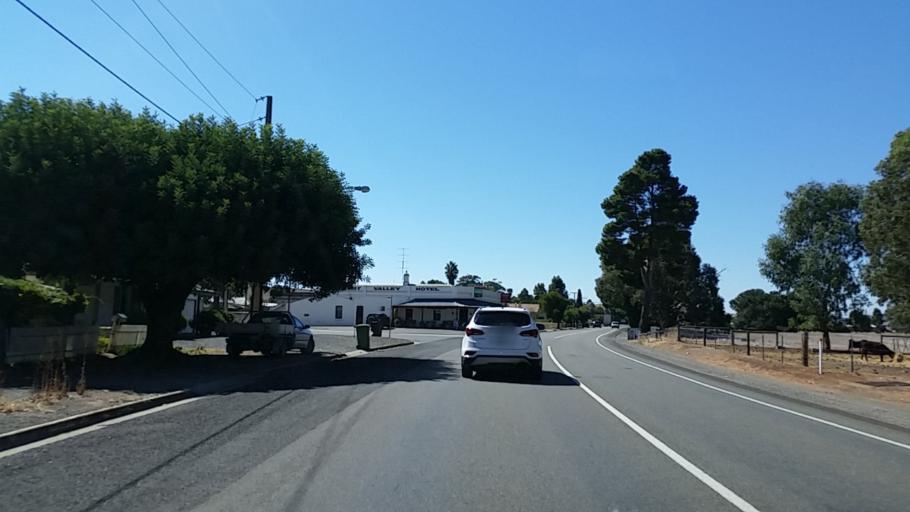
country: AU
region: South Australia
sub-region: Light
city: Kapunda
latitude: -34.0793
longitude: 138.7816
